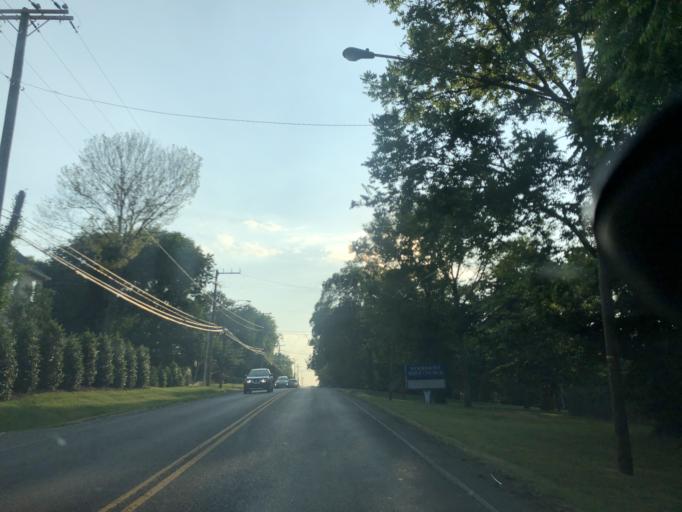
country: US
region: Tennessee
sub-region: Davidson County
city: Oak Hill
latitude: 36.1134
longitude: -86.8037
